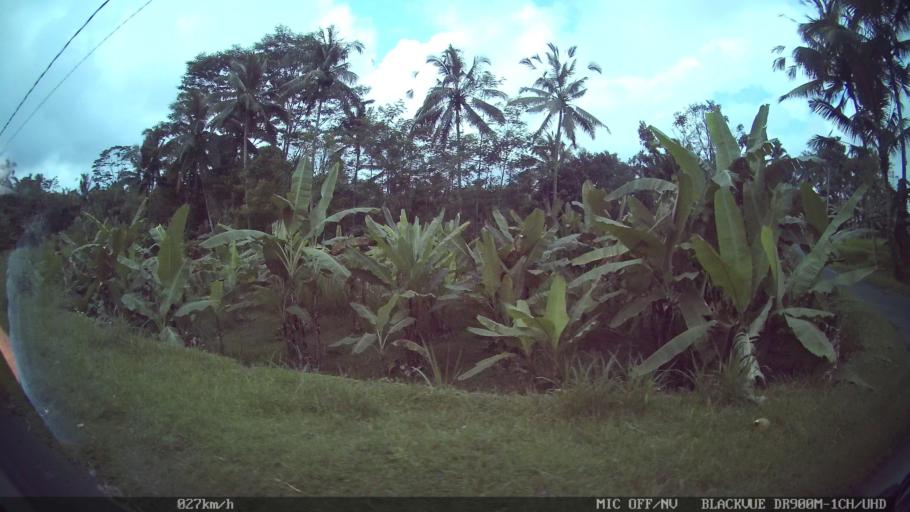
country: ID
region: Bali
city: Badung
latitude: -8.4318
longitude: 115.2261
